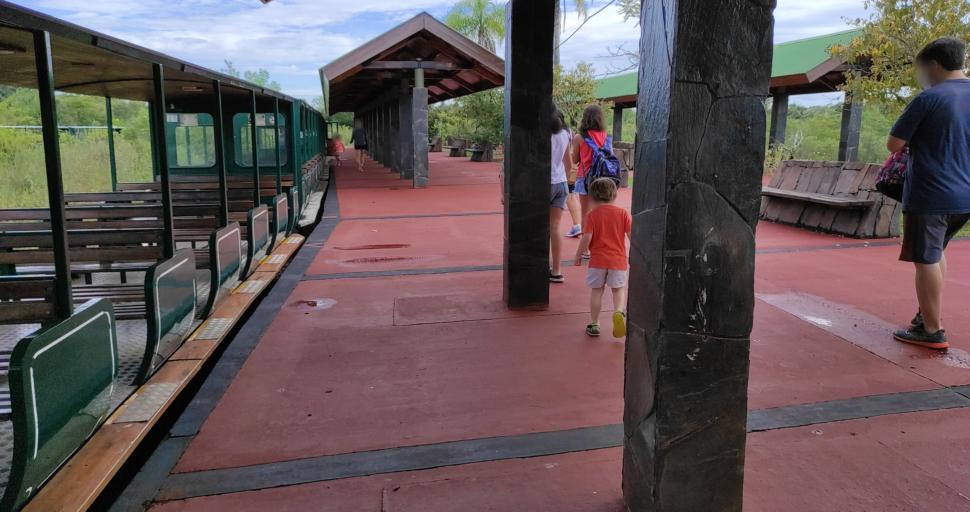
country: AR
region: Misiones
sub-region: Departamento de Iguazu
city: Puerto Iguazu
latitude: -25.6788
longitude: -54.4533
